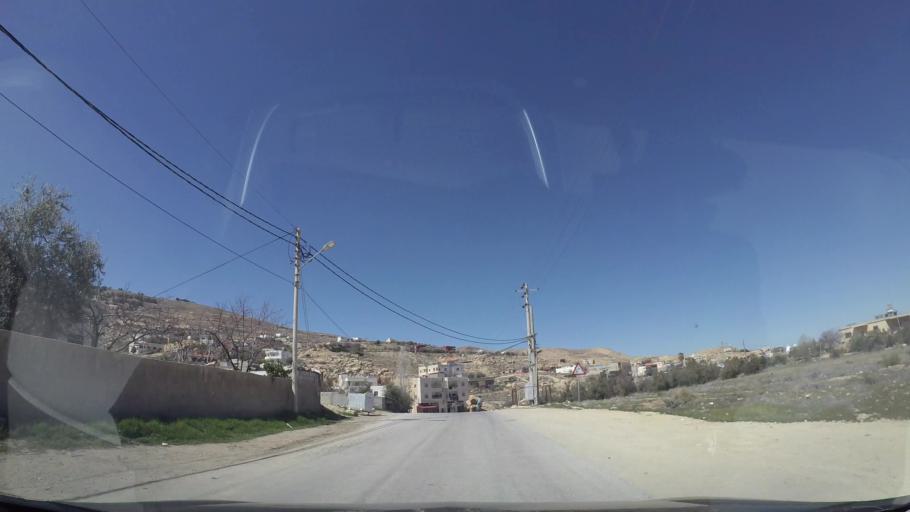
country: JO
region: Tafielah
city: At Tafilah
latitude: 30.8207
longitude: 35.5828
